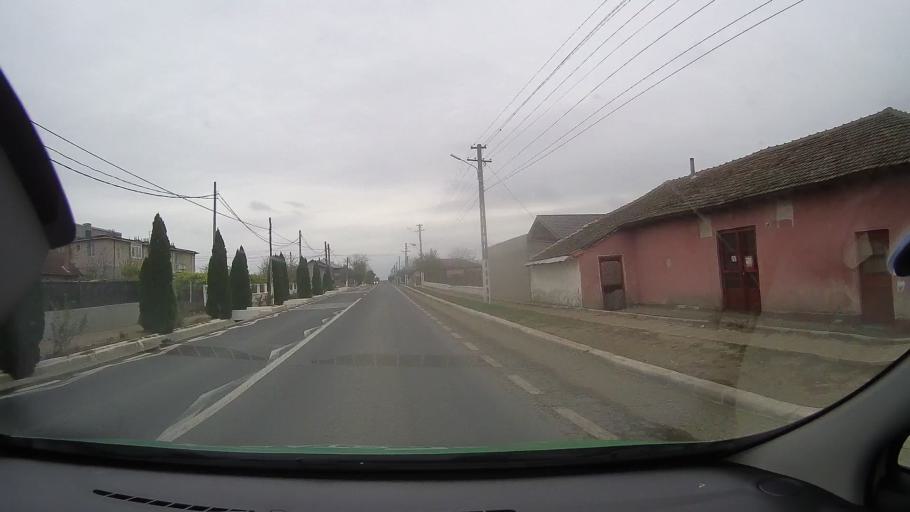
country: RO
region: Constanta
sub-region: Comuna Nicolae Balcescu
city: Nicolae Balcescu
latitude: 44.3879
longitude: 28.3814
